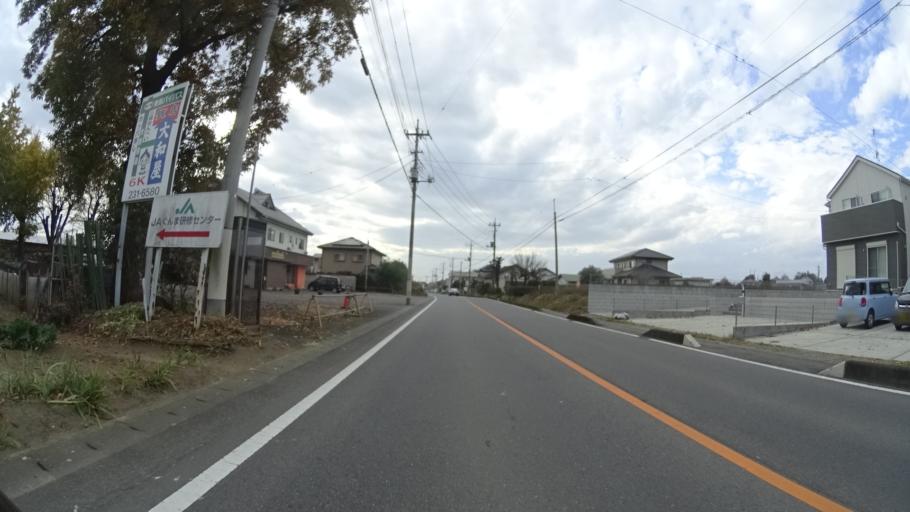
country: JP
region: Gunma
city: Maebashi-shi
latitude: 36.4103
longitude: 139.1380
